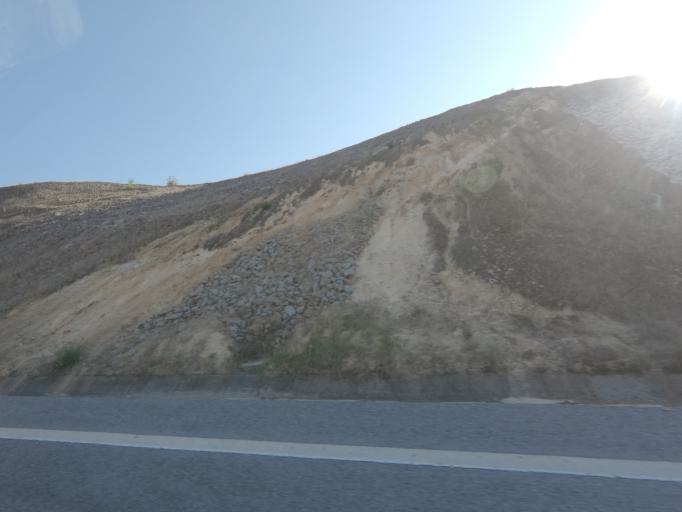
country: PT
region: Vila Real
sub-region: Chaves
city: Chaves
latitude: 41.8063
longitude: -7.4127
